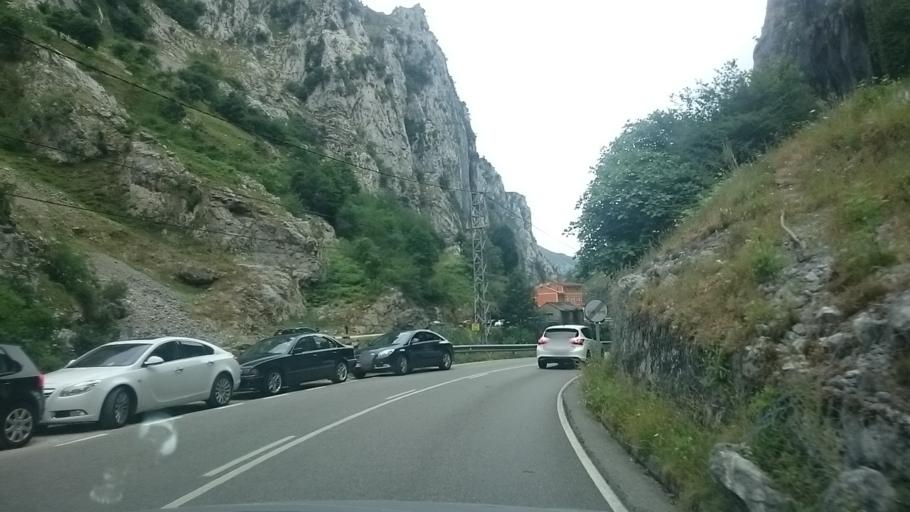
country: ES
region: Asturias
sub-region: Province of Asturias
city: Carrena
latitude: 43.2603
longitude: -4.8310
